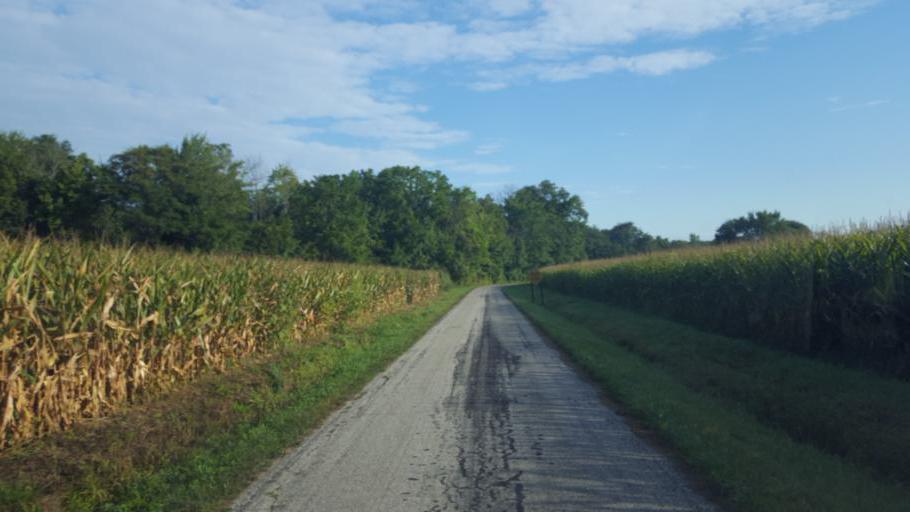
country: US
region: Ohio
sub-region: Morrow County
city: Mount Gilead
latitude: 40.6289
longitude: -82.8802
